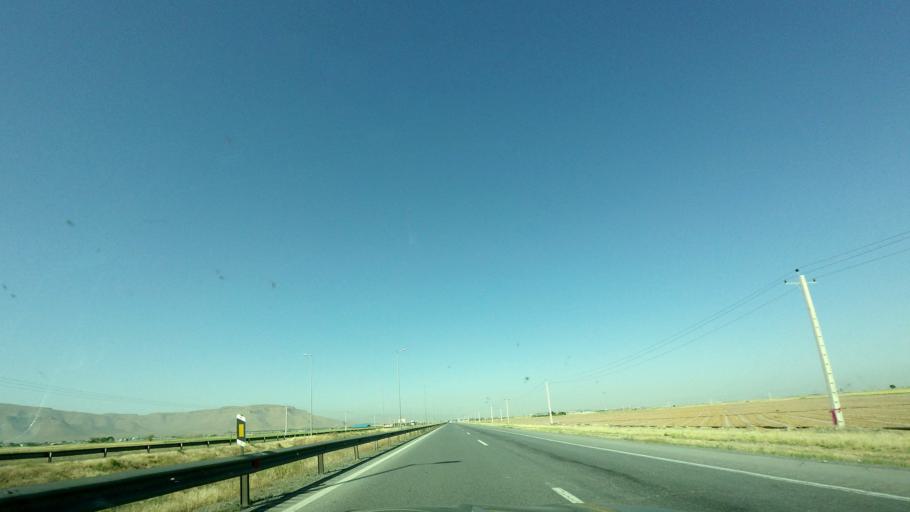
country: IR
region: Markazi
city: Arak
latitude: 34.1608
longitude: 50.0155
